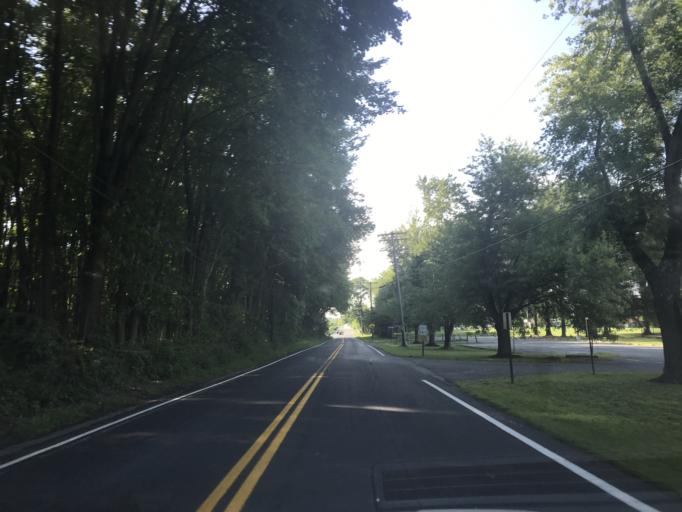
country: US
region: Maryland
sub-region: Harford County
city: Aberdeen
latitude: 39.5215
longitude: -76.1364
